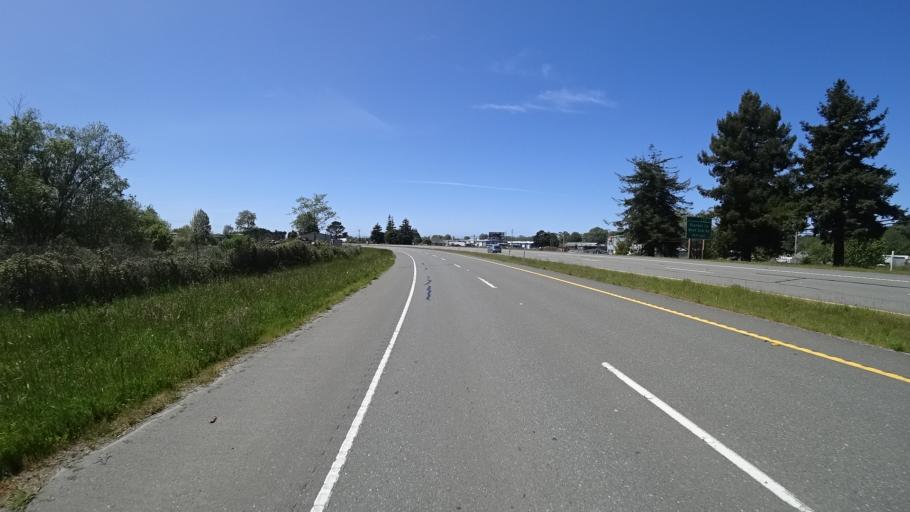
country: US
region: California
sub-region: Humboldt County
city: Arcata
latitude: 40.9100
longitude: -124.0693
